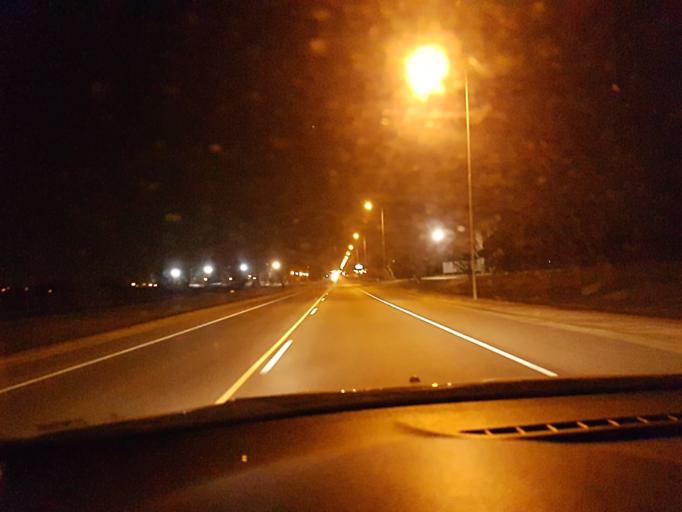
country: AR
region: Cordoba
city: Villa Allende
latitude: -31.3012
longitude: -64.2680
